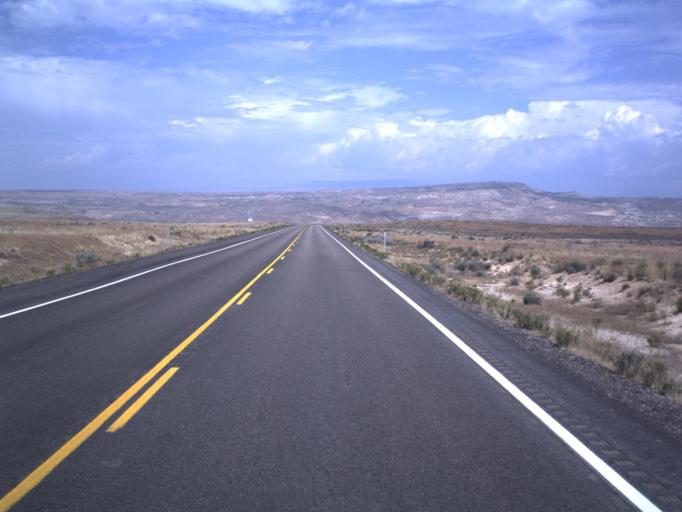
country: US
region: Utah
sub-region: Uintah County
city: Naples
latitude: 40.2815
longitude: -109.4675
